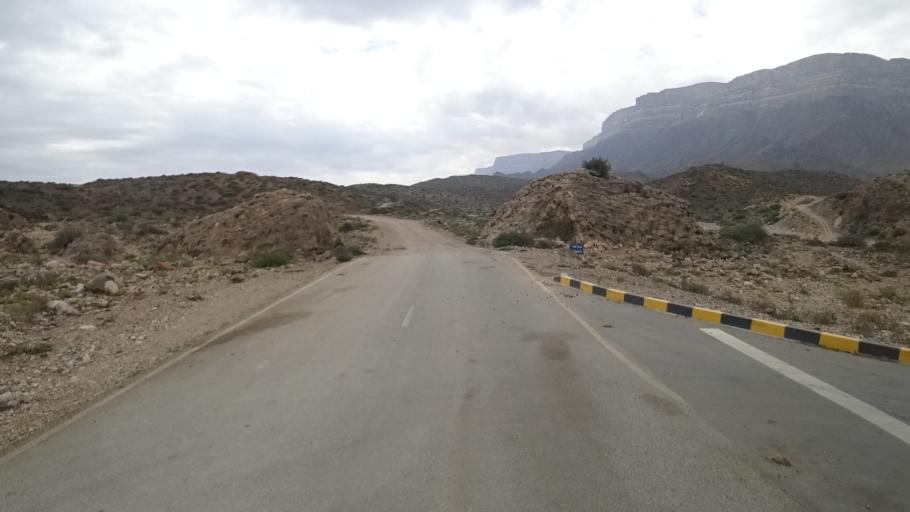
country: OM
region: Zufar
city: Salalah
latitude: 17.1728
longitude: 54.9609
